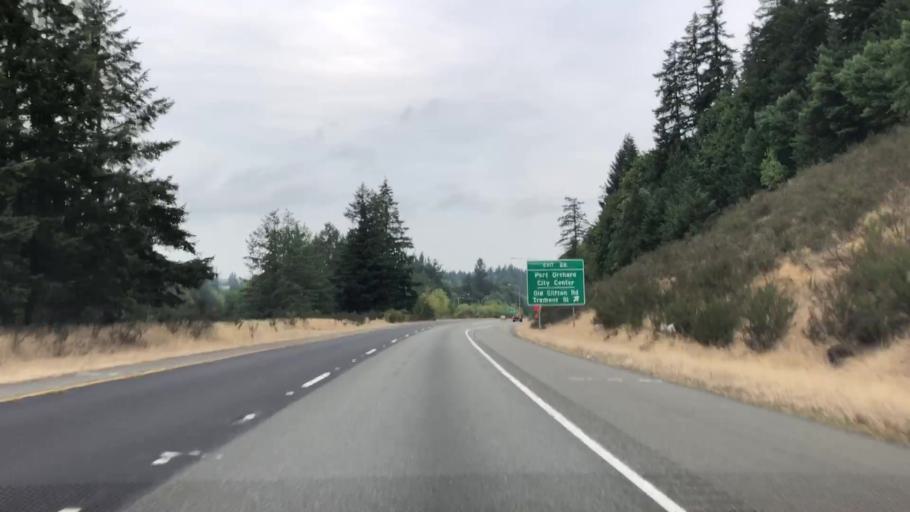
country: US
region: Washington
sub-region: Kitsap County
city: Port Orchard
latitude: 47.5173
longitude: -122.6578
